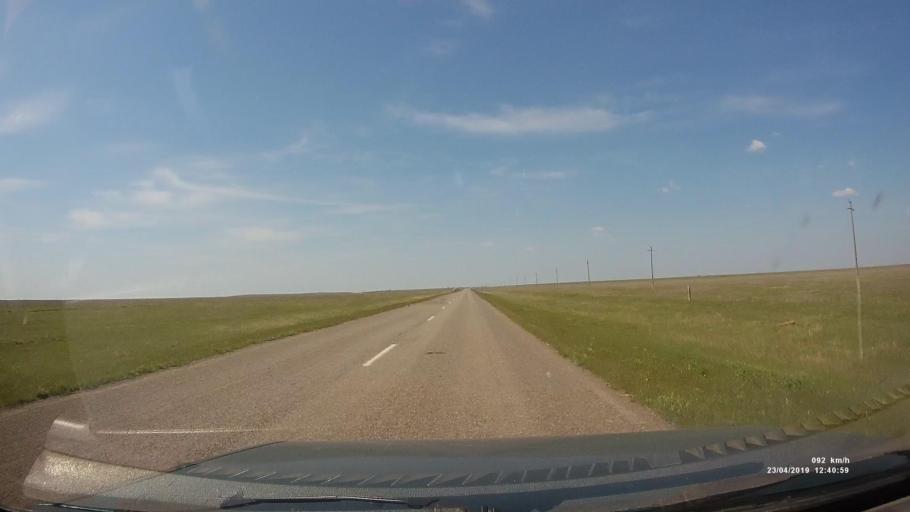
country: RU
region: Kalmykiya
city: Yashalta
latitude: 46.4447
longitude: 42.6879
